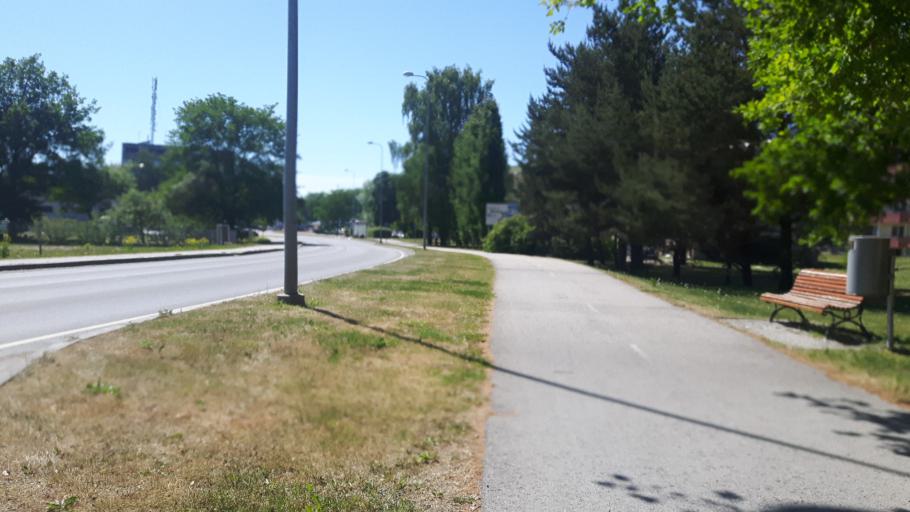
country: EE
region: Harju
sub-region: Saku vald
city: Saku
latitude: 59.3034
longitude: 24.6692
